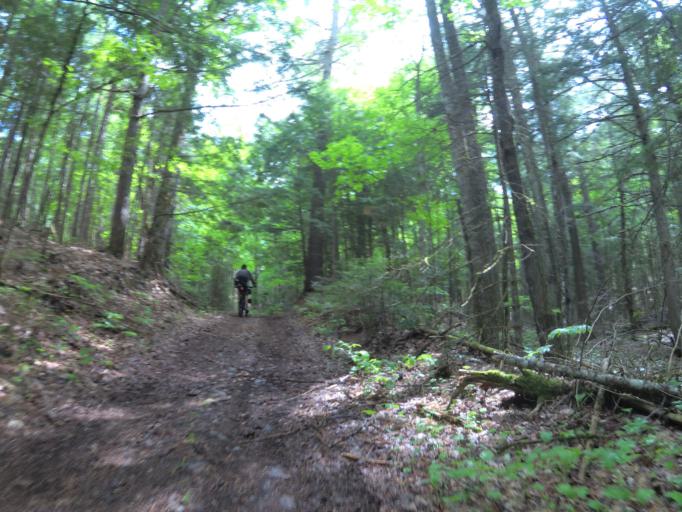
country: CA
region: Ontario
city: Renfrew
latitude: 45.1165
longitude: -76.8505
